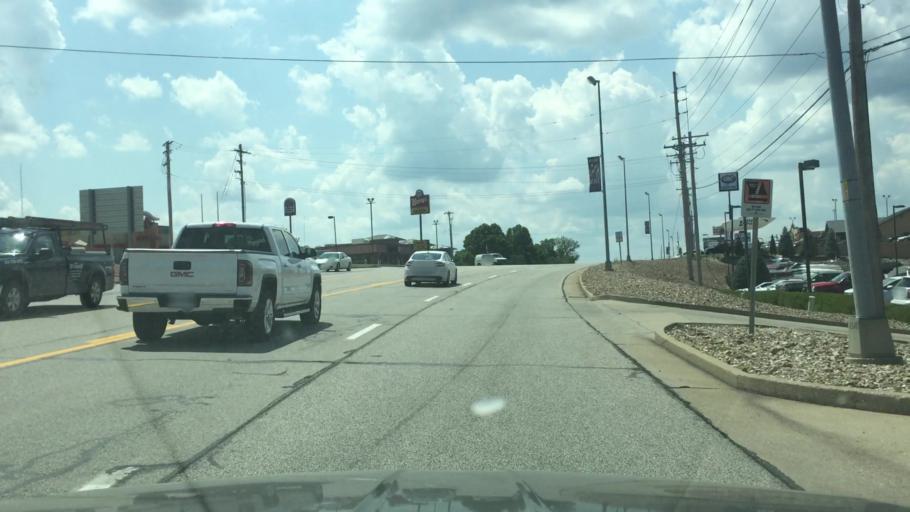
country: US
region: Missouri
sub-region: Miller County
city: Lake Ozark
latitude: 38.1703
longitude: -92.6119
